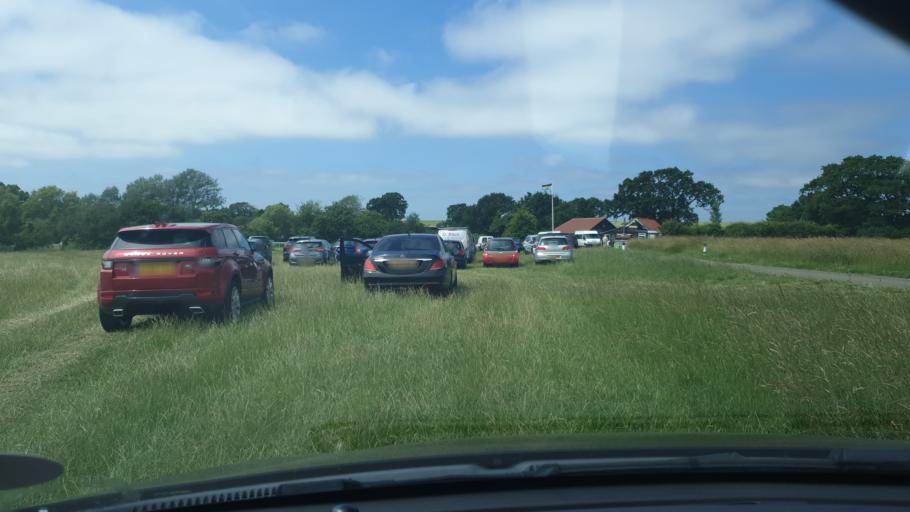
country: GB
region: England
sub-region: Essex
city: Frinton-on-Sea
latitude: 51.8342
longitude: 1.2350
